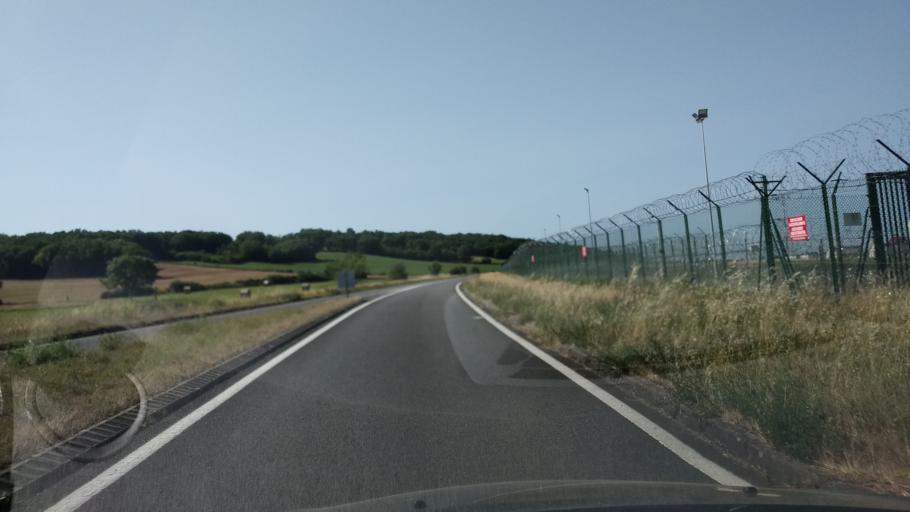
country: FR
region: Poitou-Charentes
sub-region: Departement de la Vienne
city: Lussac-les-Chateaux
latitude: 46.4496
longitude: 0.6496
